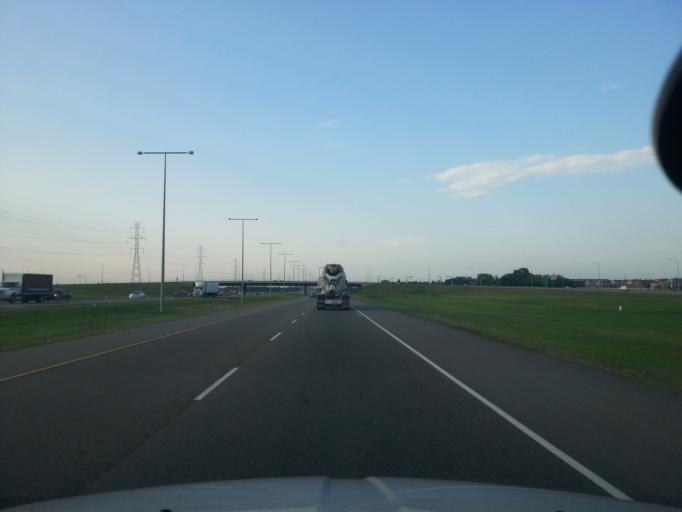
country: CA
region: Alberta
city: St. Albert
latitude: 53.4981
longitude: -113.6597
